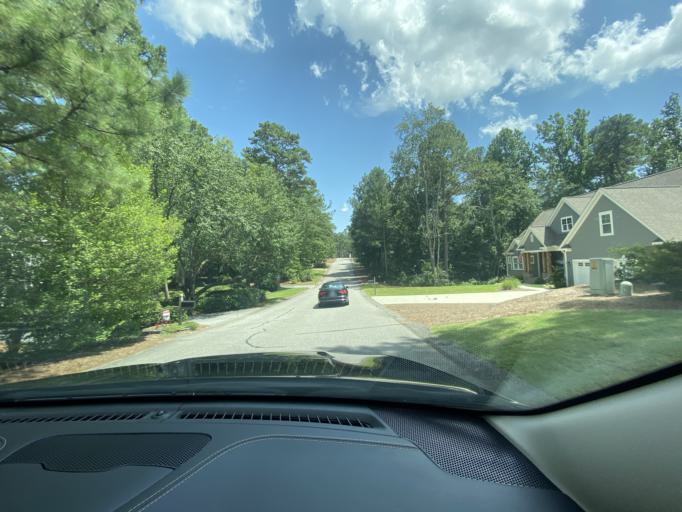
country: US
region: North Carolina
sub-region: Moore County
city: Pinehurst
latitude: 35.1986
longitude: -79.4396
